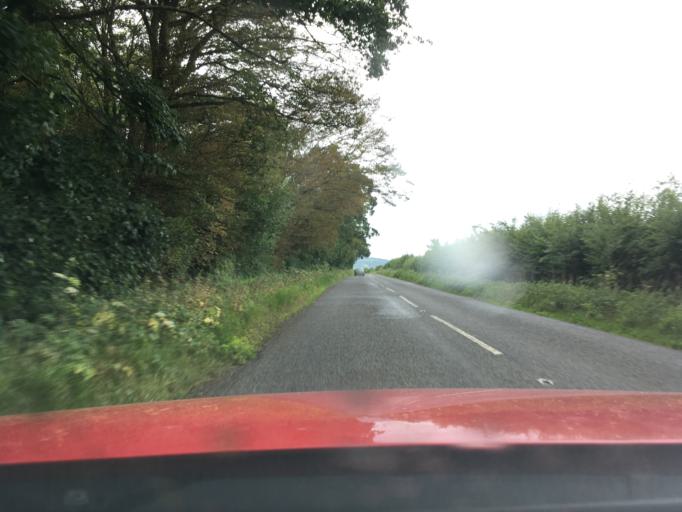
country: GB
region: England
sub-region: Gloucestershire
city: Winchcombe
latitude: 52.0027
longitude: -1.9609
